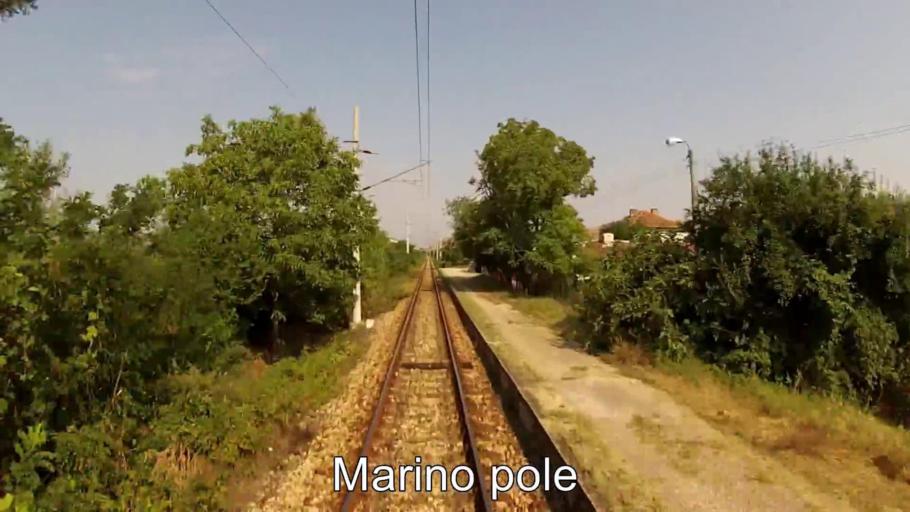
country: BG
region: Blagoevgrad
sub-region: Obshtina Petrich
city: Petrich
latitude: 41.4150
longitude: 23.3381
